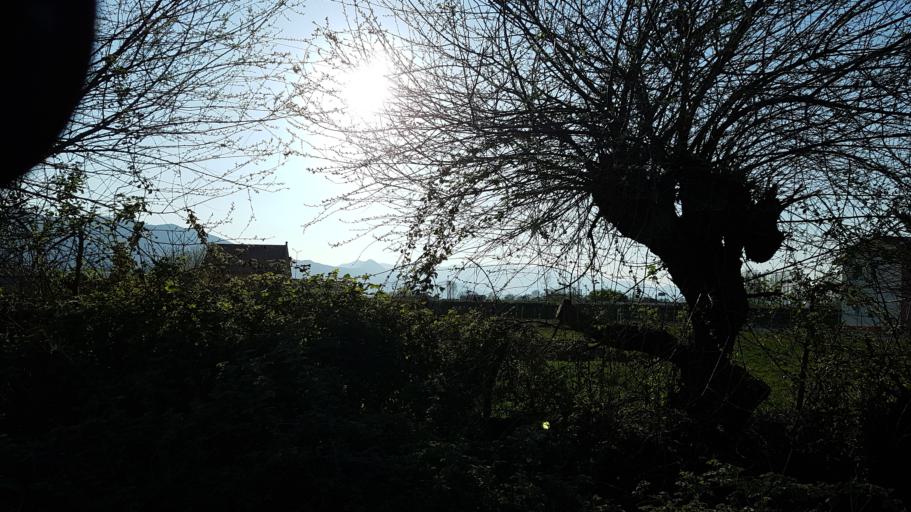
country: AL
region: Shkoder
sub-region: Rrethi i Shkodres
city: Shkoder
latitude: 42.0787
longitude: 19.4938
